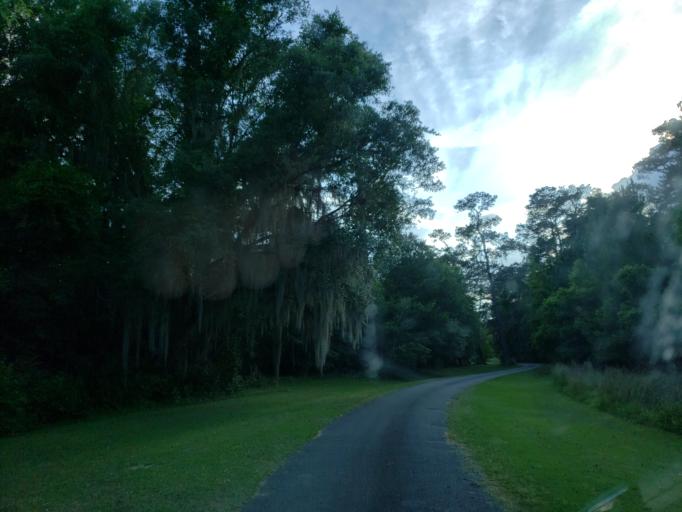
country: US
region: Georgia
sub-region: Cook County
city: Adel
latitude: 31.1256
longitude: -83.4146
